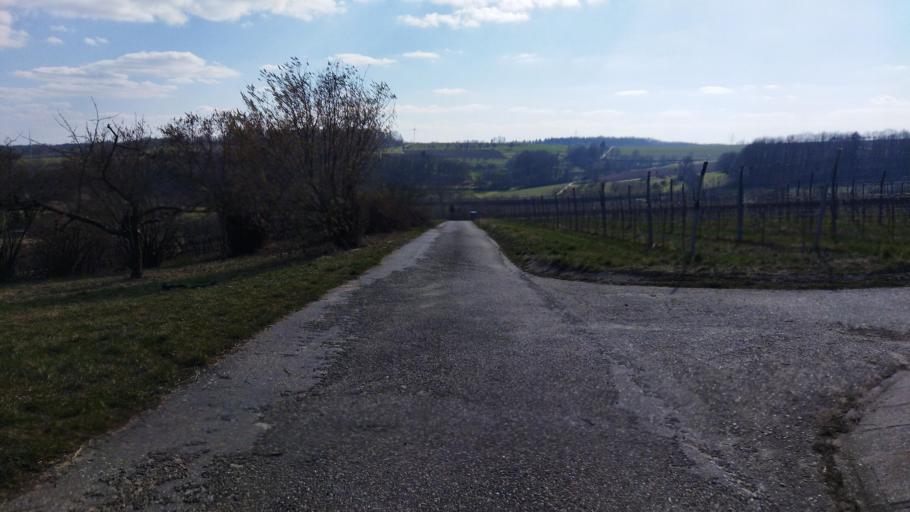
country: DE
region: Baden-Wuerttemberg
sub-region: Regierungsbezirk Stuttgart
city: Ilsfeld
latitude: 49.0572
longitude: 9.2244
